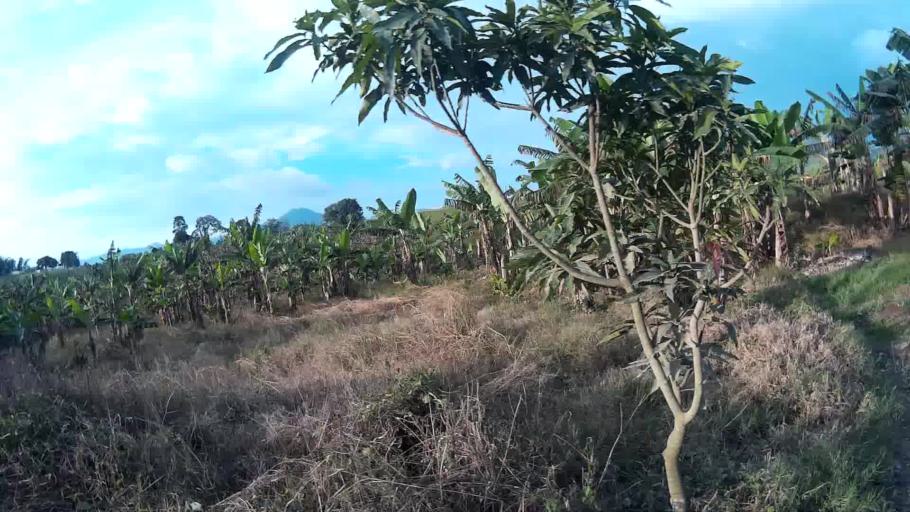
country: CO
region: Valle del Cauca
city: Ulloa
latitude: 4.7636
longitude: -75.7487
